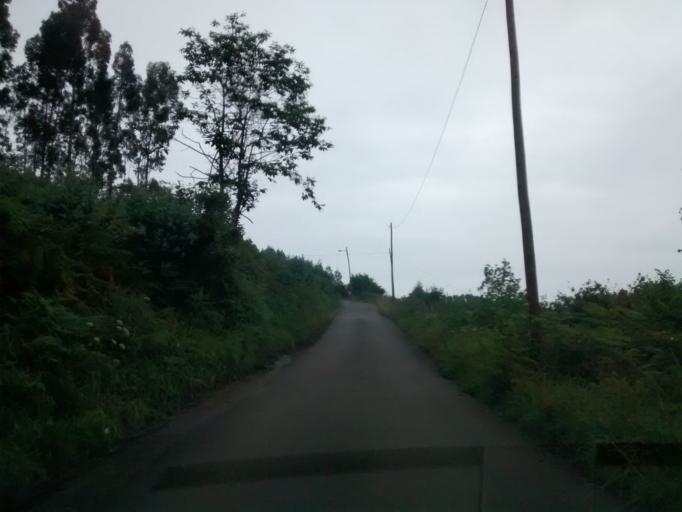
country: ES
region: Asturias
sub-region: Province of Asturias
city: Villaviciosa
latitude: 43.5408
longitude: -5.4082
